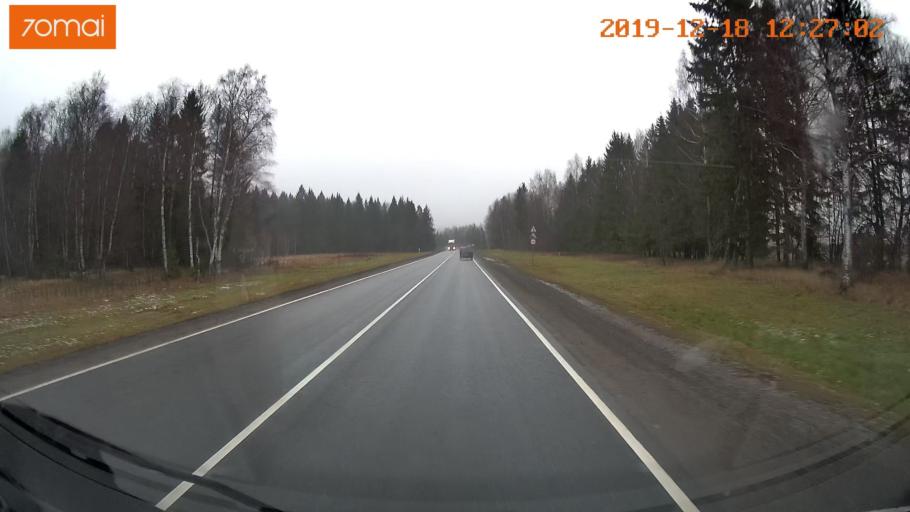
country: RU
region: Moskovskaya
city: Novopetrovskoye
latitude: 56.0578
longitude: 36.5028
